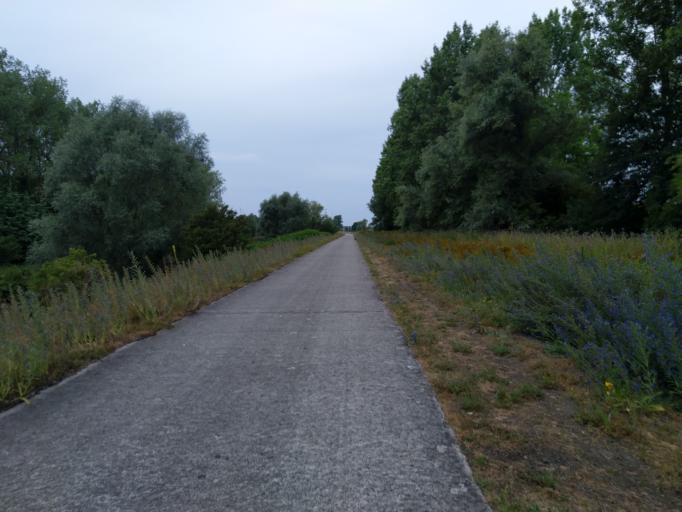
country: BE
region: Wallonia
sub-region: Province du Hainaut
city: Hensies
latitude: 50.4521
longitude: 3.7327
